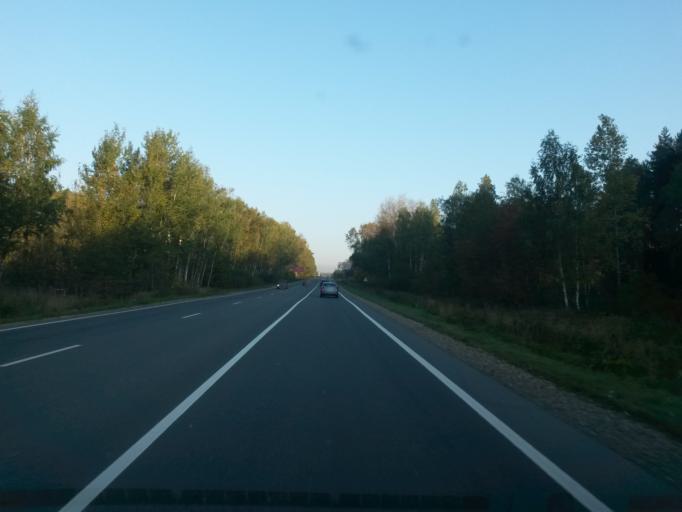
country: RU
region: Moskovskaya
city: Barybino
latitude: 55.2383
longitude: 37.8588
